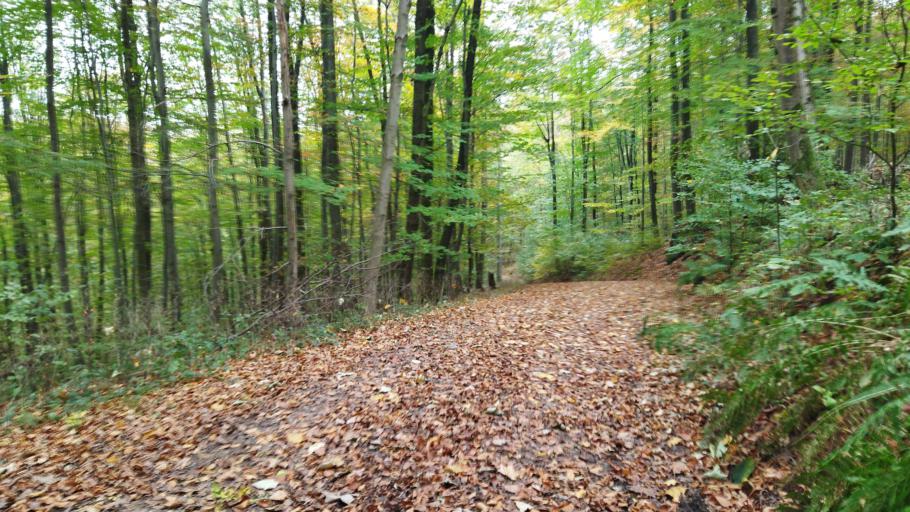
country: DE
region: Hesse
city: Lutzelbach
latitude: 49.7034
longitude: 8.7145
